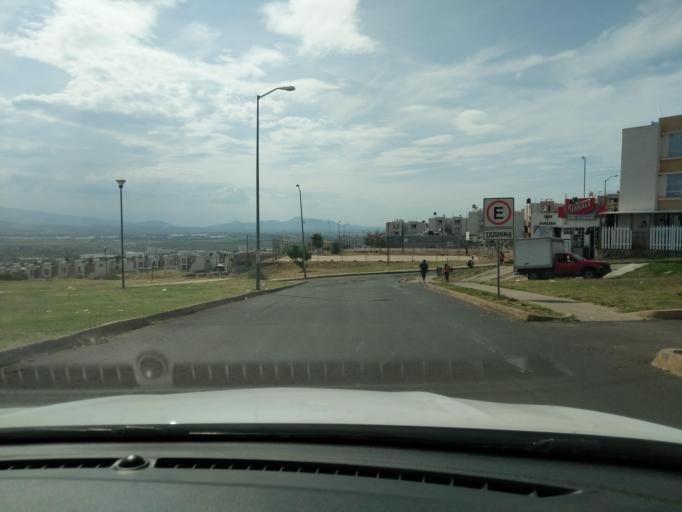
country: MX
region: Jalisco
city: San Jose del Castillo
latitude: 20.5220
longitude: -103.2231
